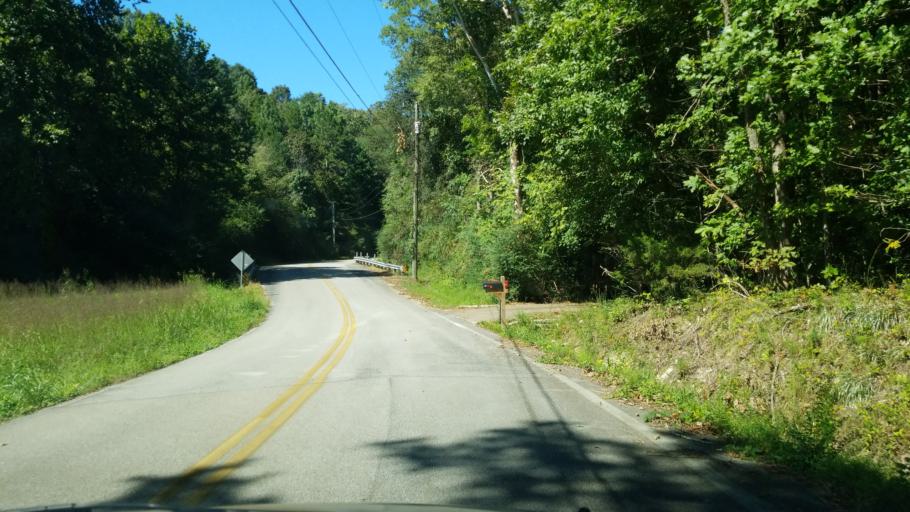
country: US
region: Tennessee
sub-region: Hamilton County
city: Harrison
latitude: 35.0986
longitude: -85.0855
